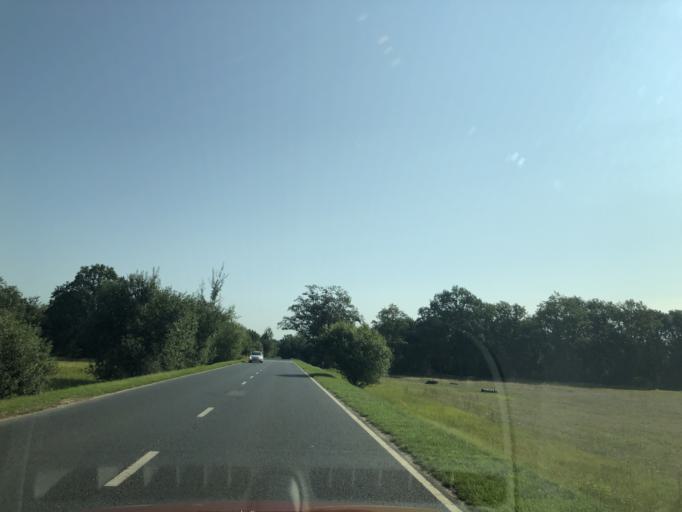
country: PL
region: Lower Silesian Voivodeship
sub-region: Powiat wroclawski
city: Smolec
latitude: 51.1694
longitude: 16.9180
